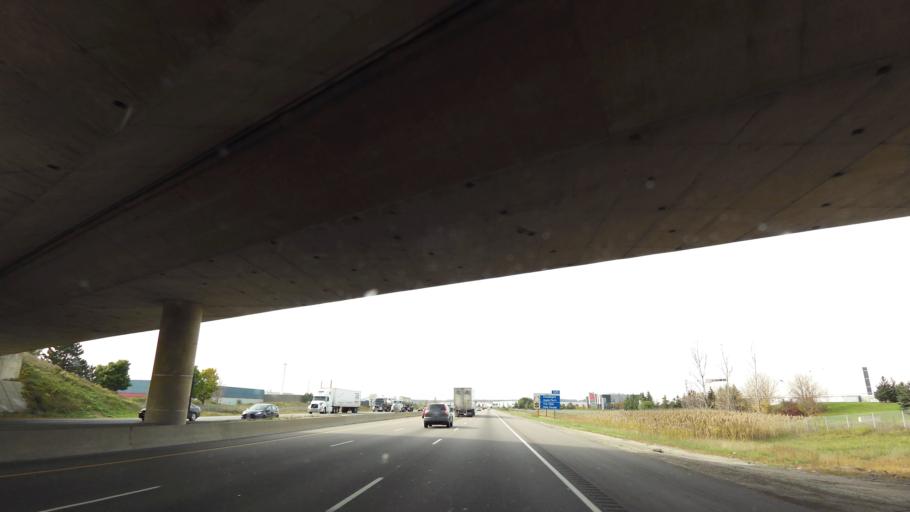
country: CA
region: Ontario
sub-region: Halton
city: Milton
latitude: 43.5385
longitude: -79.8763
